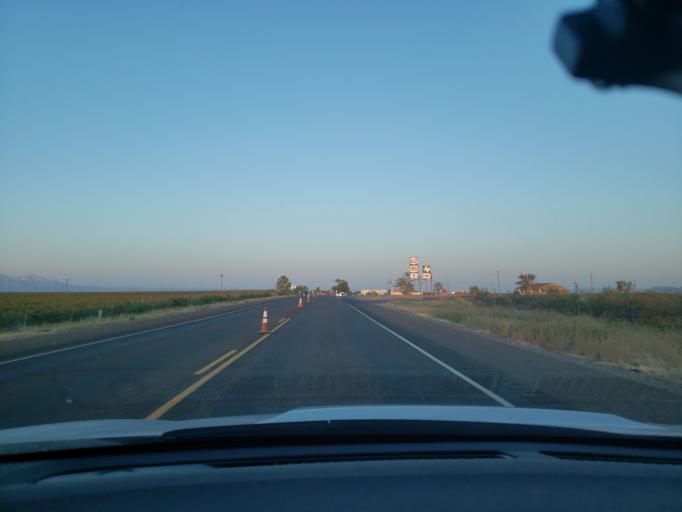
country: US
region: Texas
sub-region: Hudspeth County
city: Sierra Blanca
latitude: 31.7618
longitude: -105.3699
